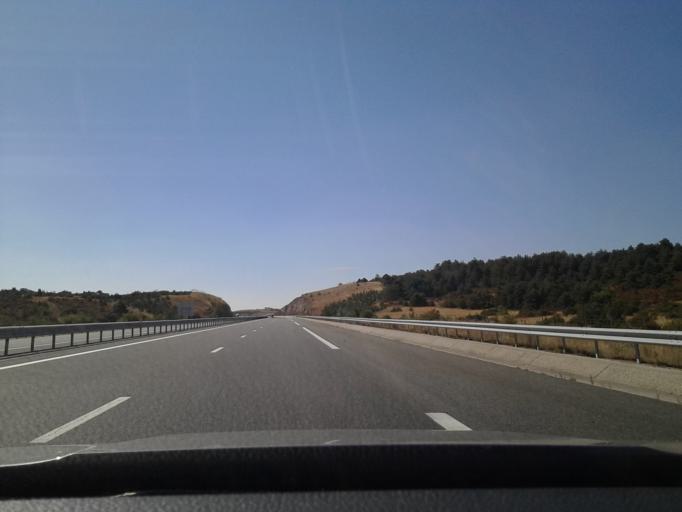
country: FR
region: Midi-Pyrenees
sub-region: Departement de l'Aveyron
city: Creissels
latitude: 44.0406
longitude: 3.0583
